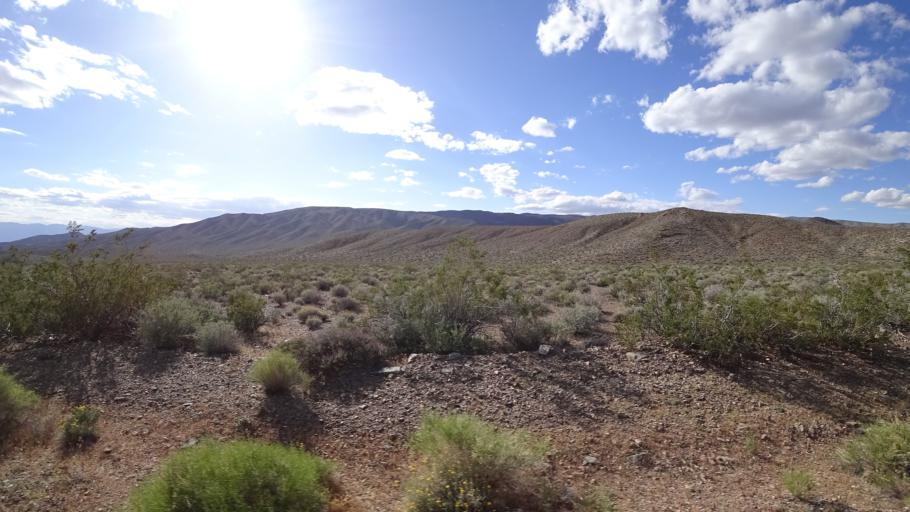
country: US
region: California
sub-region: San Bernardino County
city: Searles Valley
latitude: 36.2922
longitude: -117.1757
